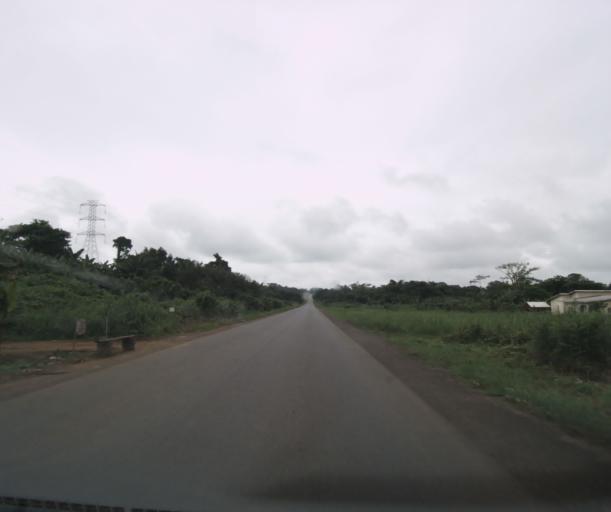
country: CM
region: Littoral
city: Edea
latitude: 3.7088
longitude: 10.1078
